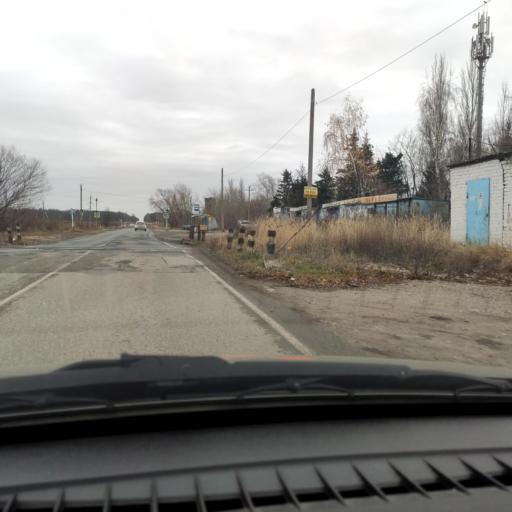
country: RU
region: Samara
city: Zhigulevsk
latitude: 53.3405
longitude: 49.4693
